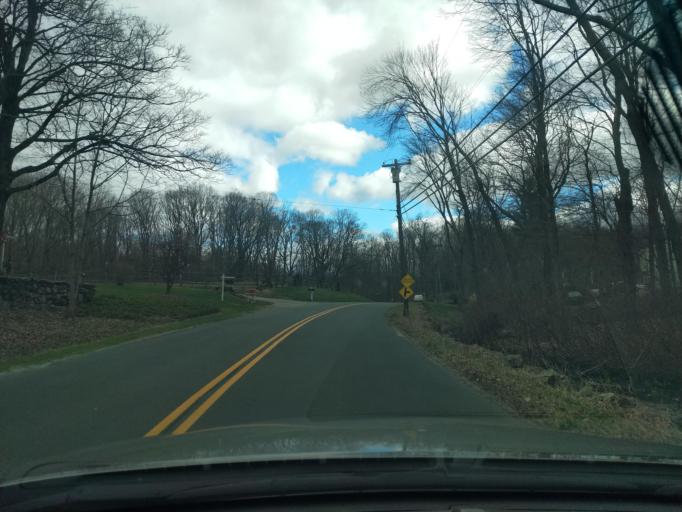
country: US
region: Connecticut
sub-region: Fairfield County
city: Newtown
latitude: 41.3494
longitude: -73.3195
